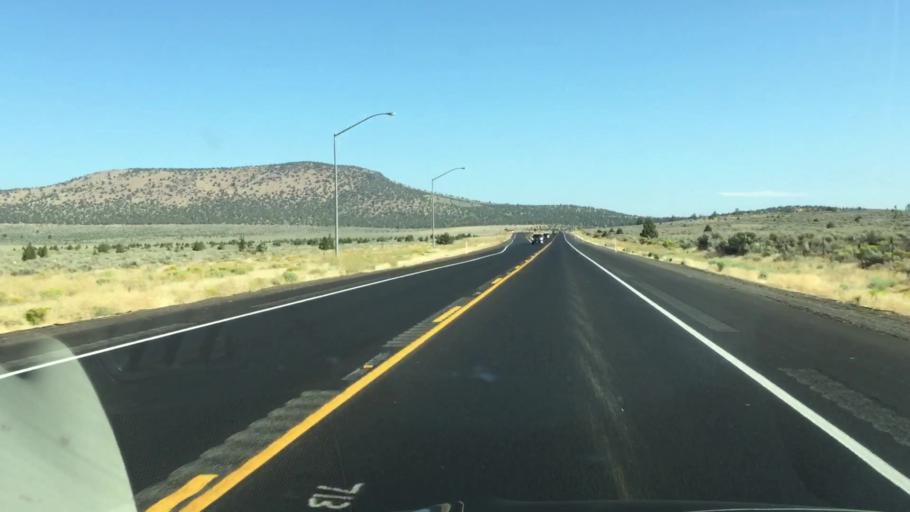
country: US
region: Oregon
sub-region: Jefferson County
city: Culver
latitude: 44.4519
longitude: -121.1995
